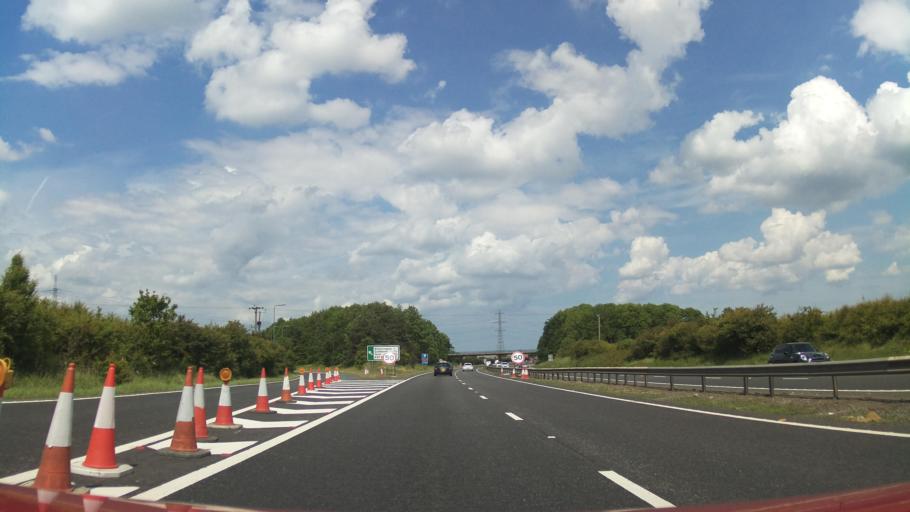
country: GB
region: England
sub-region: Stockton-on-Tees
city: Yarm
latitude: 54.4687
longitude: -1.3255
